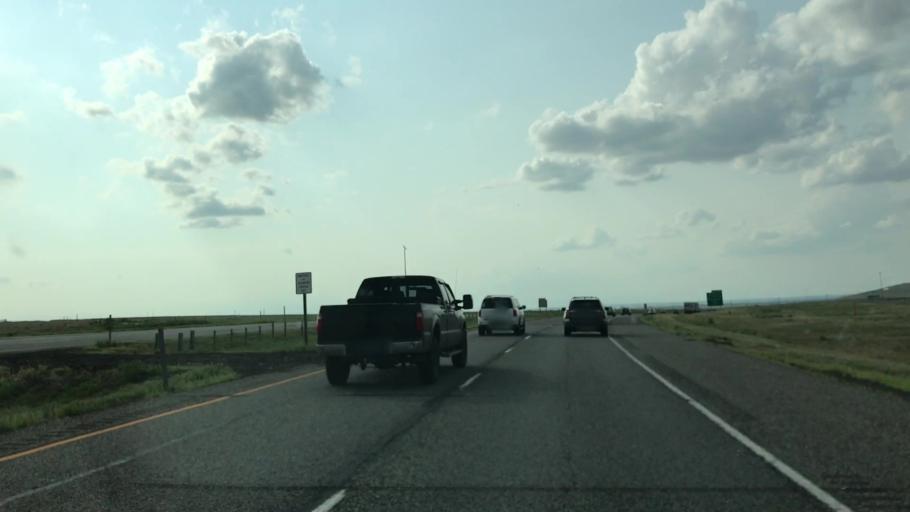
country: US
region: Colorado
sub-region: Adams County
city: Aurora
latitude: 39.8198
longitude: -104.7419
